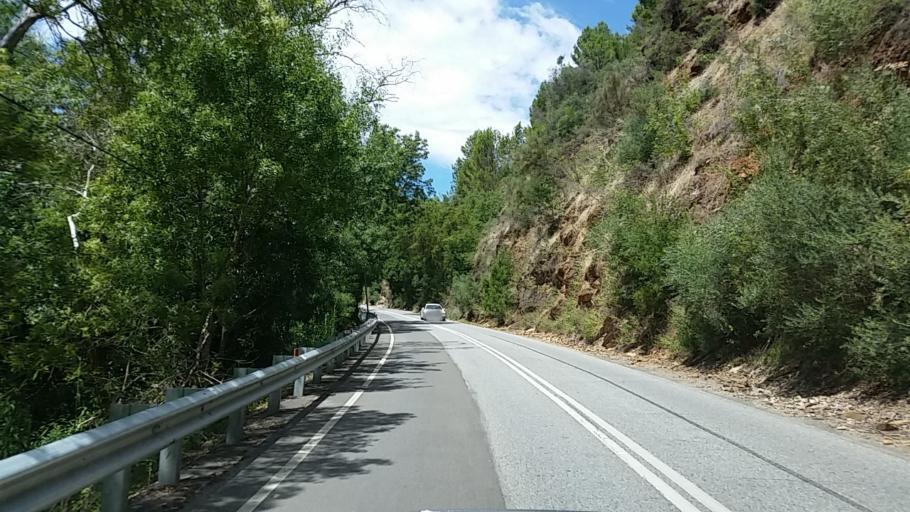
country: AU
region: South Australia
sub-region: Campbelltown
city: Athelstone
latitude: -34.8648
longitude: 138.7481
